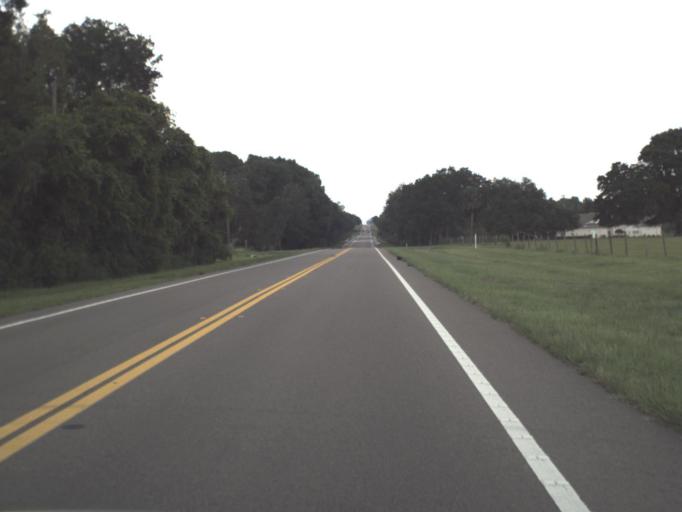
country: US
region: Florida
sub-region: Hillsborough County
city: Balm
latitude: 27.7047
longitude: -82.1889
